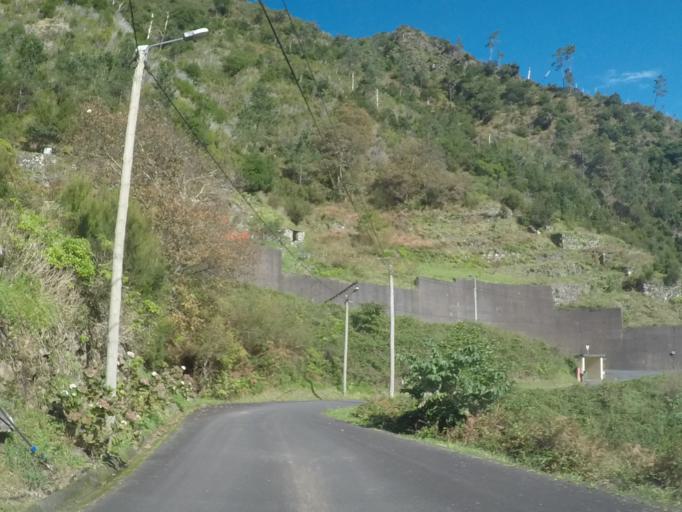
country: PT
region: Madeira
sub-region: Camara de Lobos
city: Curral das Freiras
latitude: 32.7842
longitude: -16.9776
